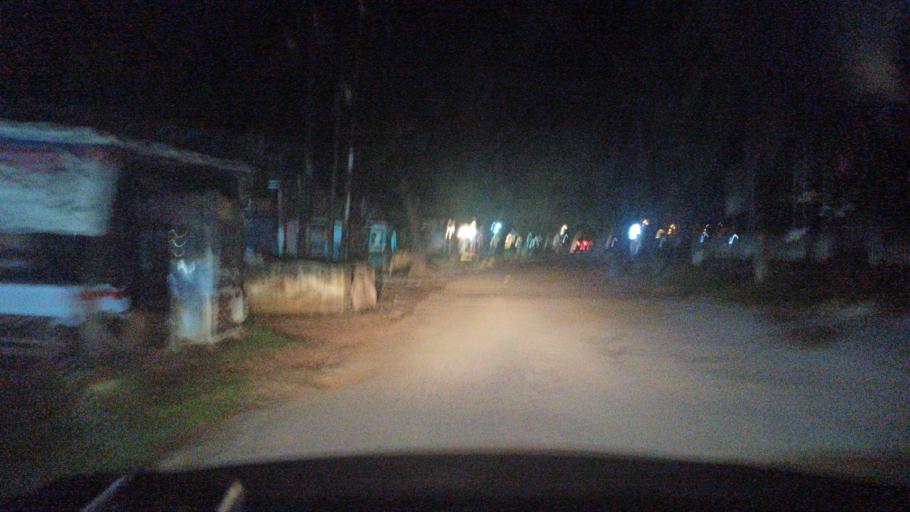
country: ID
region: South Sumatra
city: Plaju
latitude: -2.9916
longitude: 104.7477
